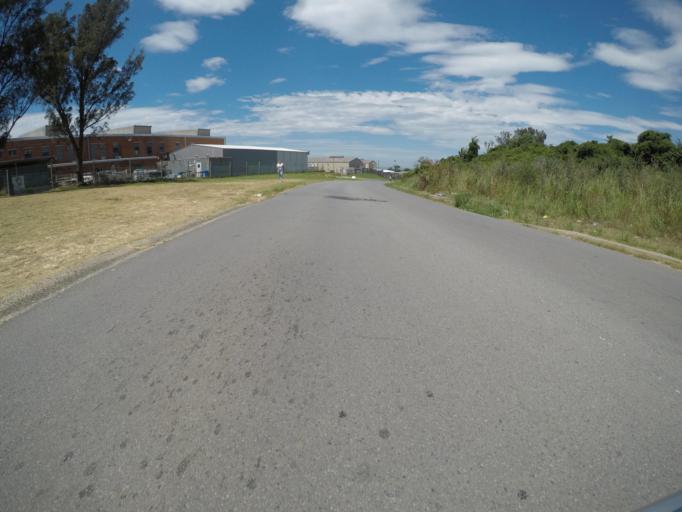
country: ZA
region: Eastern Cape
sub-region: Buffalo City Metropolitan Municipality
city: East London
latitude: -33.0365
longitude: 27.8691
